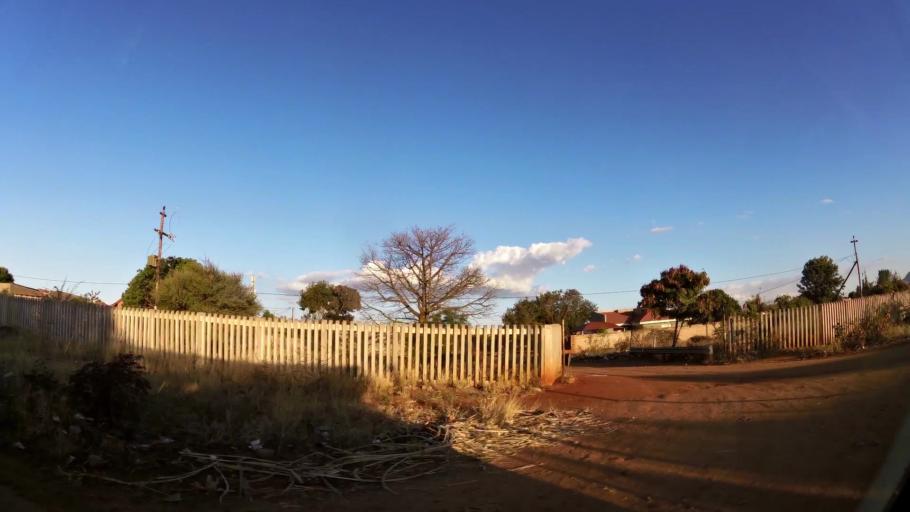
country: ZA
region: Limpopo
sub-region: Waterberg District Municipality
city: Mokopane
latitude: -24.1407
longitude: 28.9958
